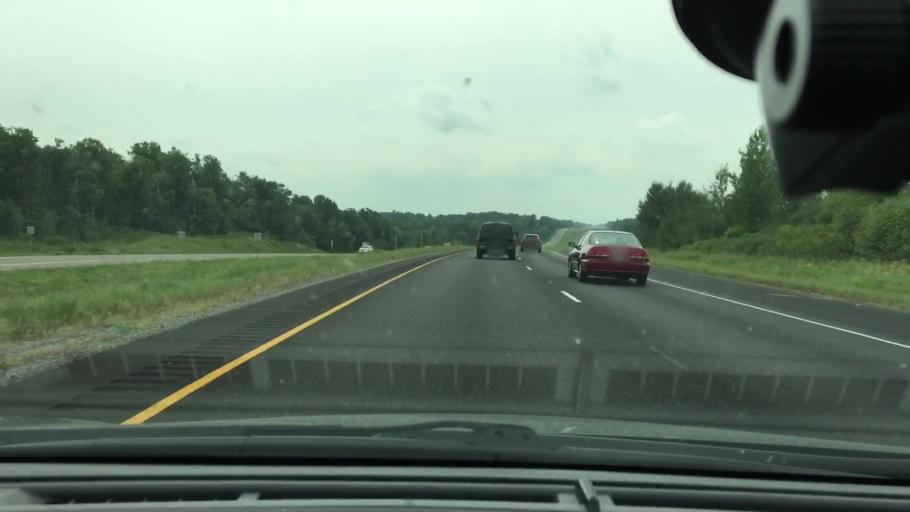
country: US
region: Minnesota
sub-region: Mille Lacs County
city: Milaca
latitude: 45.8216
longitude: -93.6557
